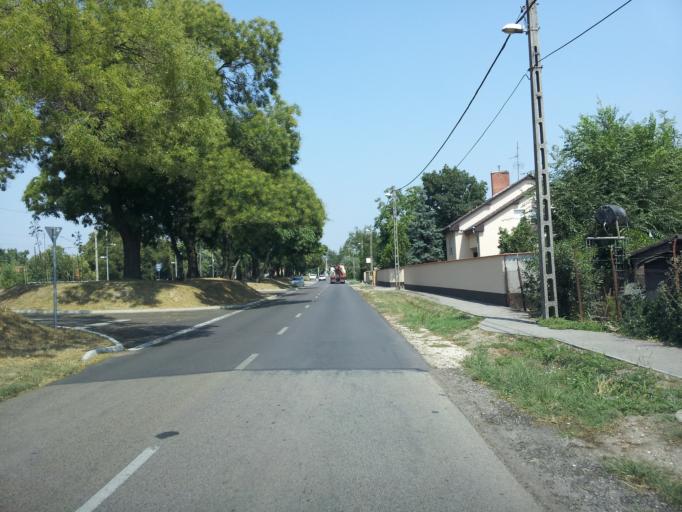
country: HU
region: Pest
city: Dunavarsany
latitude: 47.2724
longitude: 19.0649
